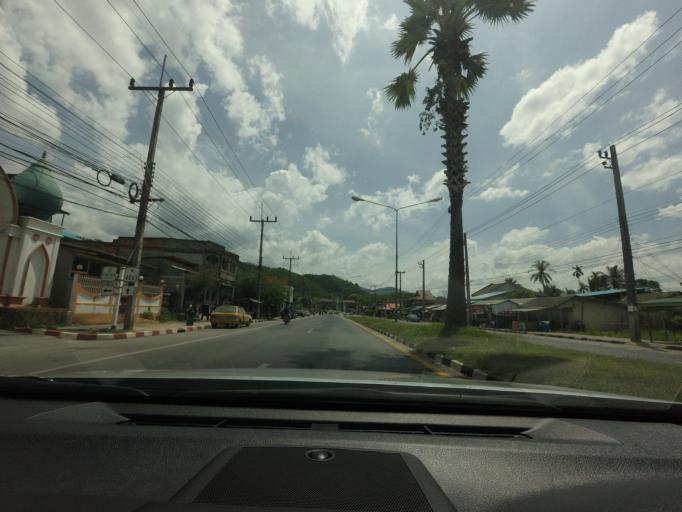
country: TH
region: Yala
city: Krong Pi Nang
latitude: 6.4583
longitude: 101.3359
